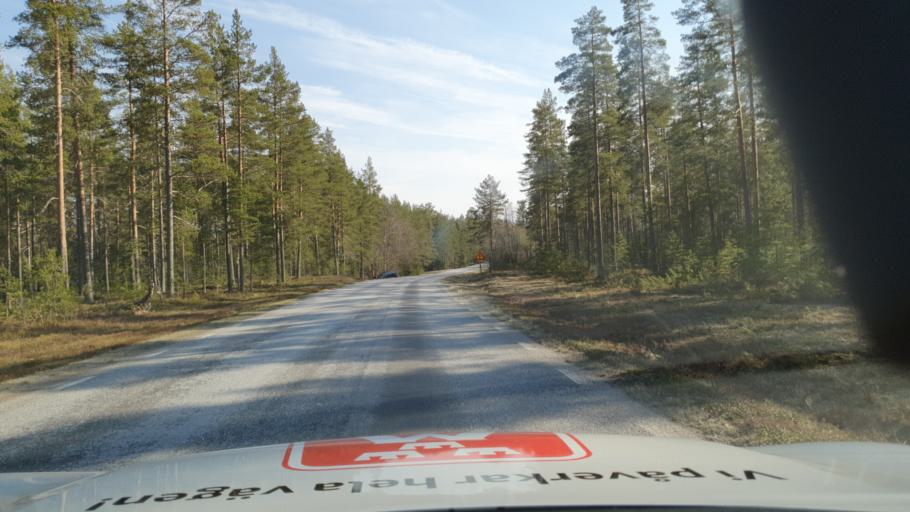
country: SE
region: Vaesterbotten
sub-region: Umea Kommun
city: Roback
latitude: 63.8924
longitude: 20.1574
